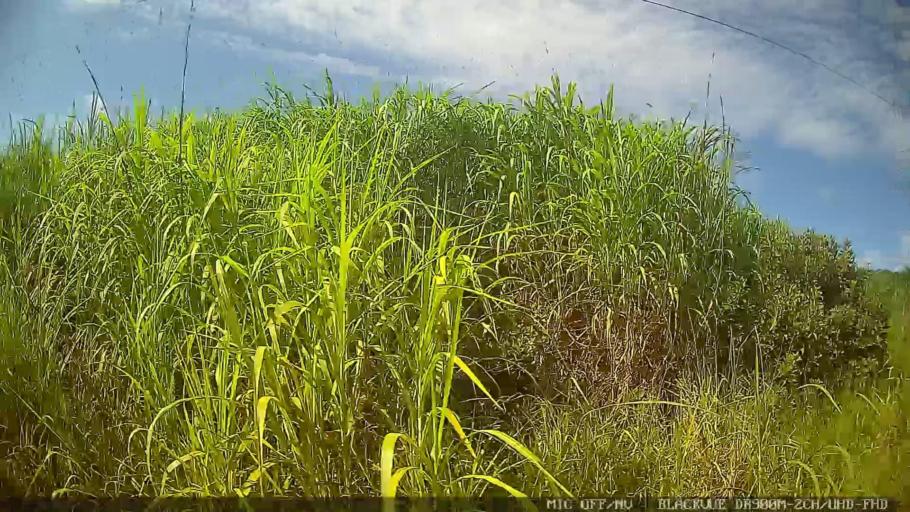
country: BR
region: Sao Paulo
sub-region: Jarinu
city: Jarinu
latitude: -23.0709
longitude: -46.6658
